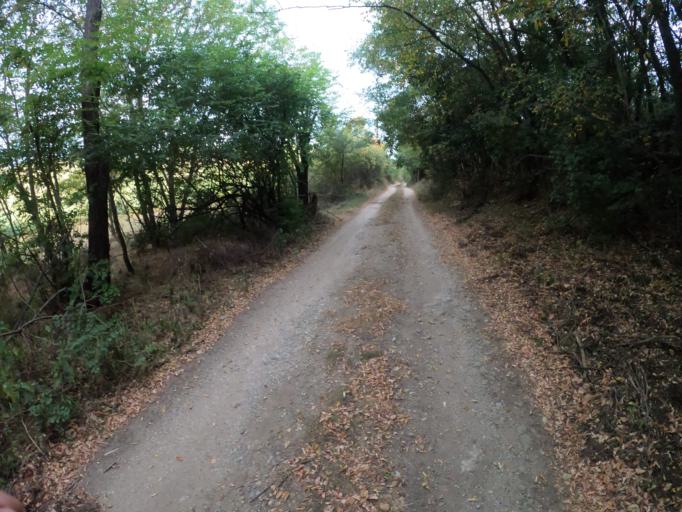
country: HU
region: Veszprem
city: Revfueloep
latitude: 46.8915
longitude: 17.5598
